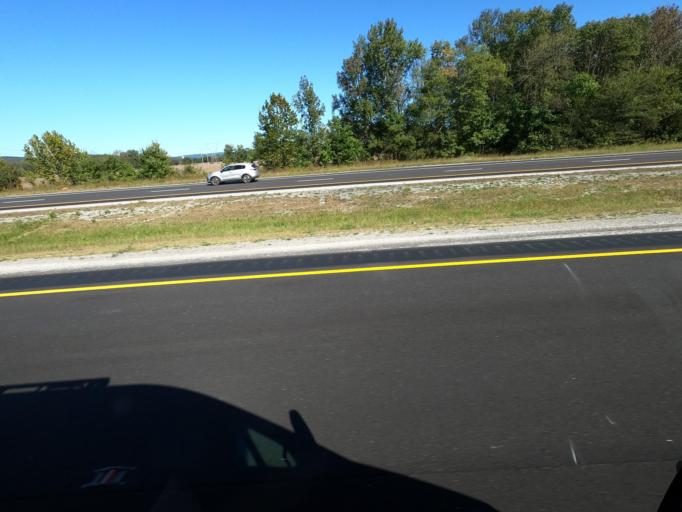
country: US
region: Tennessee
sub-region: Marion County
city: Monteagle
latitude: 35.2935
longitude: -85.8976
